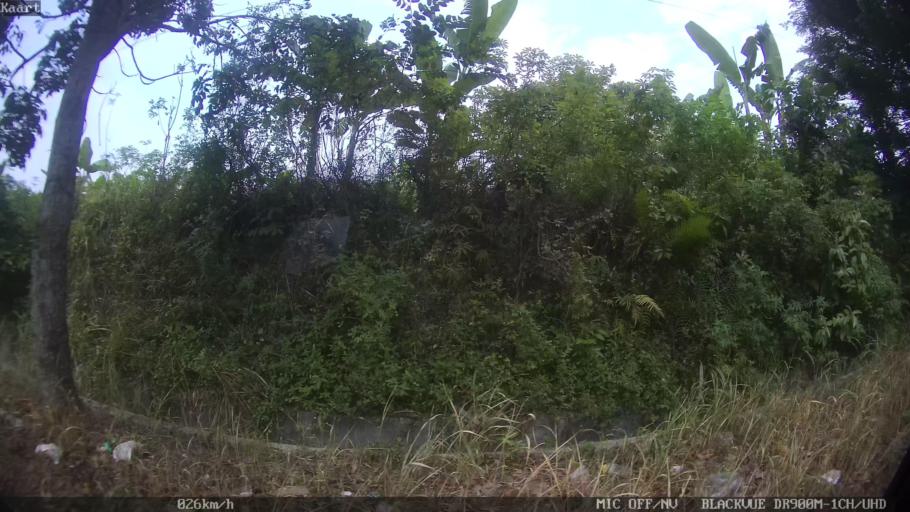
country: ID
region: Lampung
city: Bandarlampung
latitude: -5.4443
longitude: 105.2426
